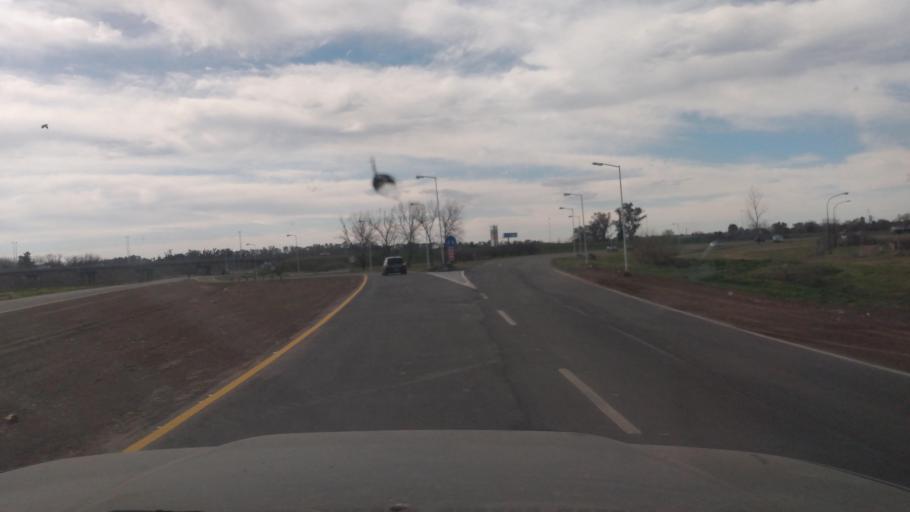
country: AR
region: Buenos Aires
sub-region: Partido de Lujan
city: Lujan
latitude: -34.5520
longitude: -59.1161
